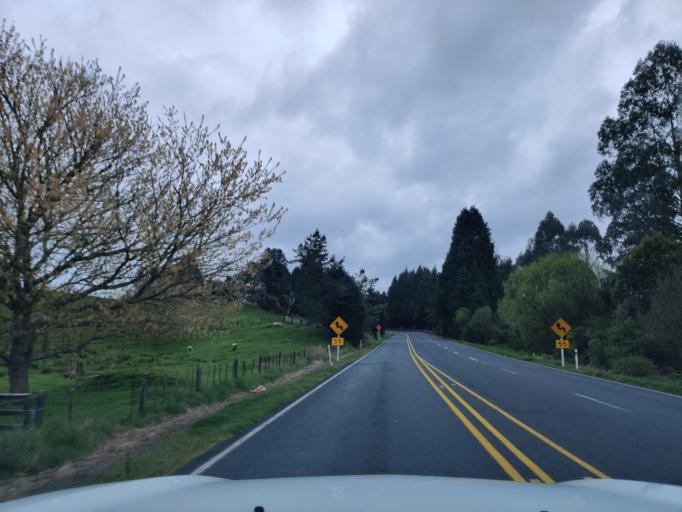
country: NZ
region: Waikato
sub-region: Otorohanga District
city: Otorohanga
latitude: -38.5011
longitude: 175.2021
